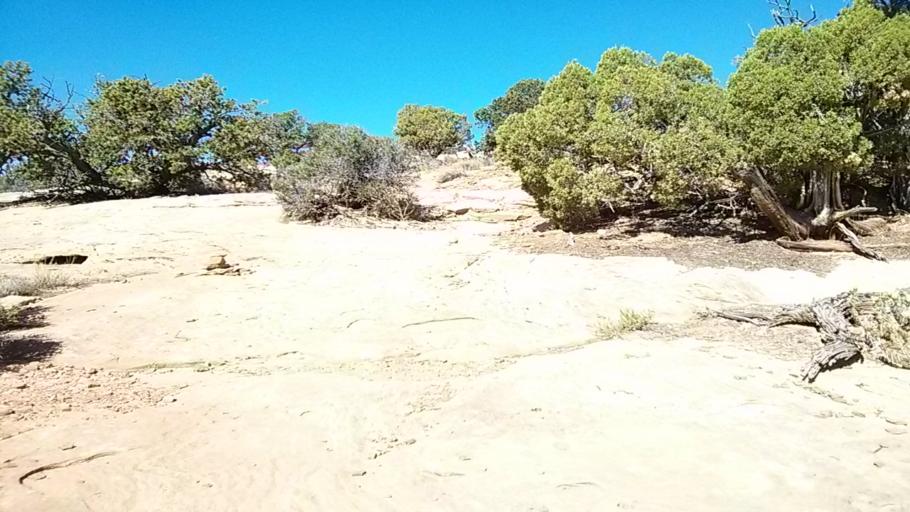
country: US
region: Utah
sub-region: Wayne County
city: Loa
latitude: 38.2915
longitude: -111.2387
